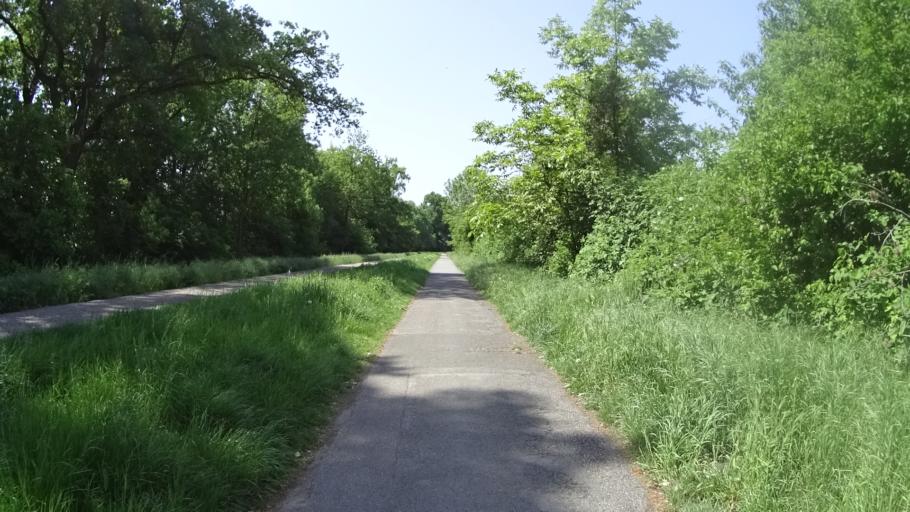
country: DE
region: Rheinland-Pfalz
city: Altrip
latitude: 49.4452
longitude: 8.4704
